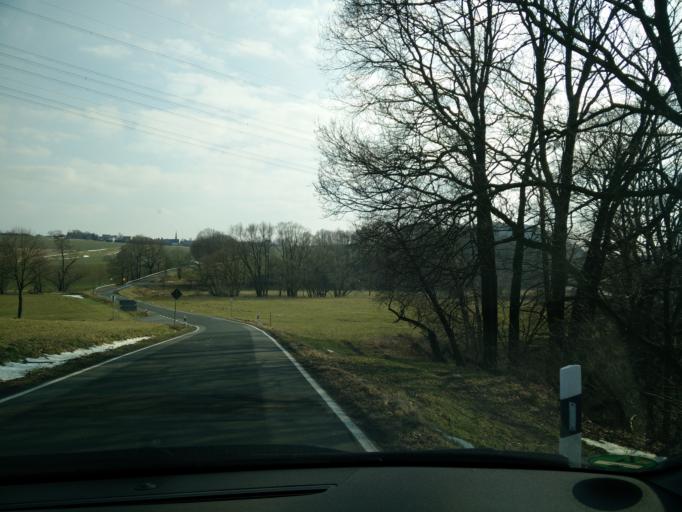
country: DE
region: Saxony
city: Colditz
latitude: 51.1130
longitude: 12.8156
